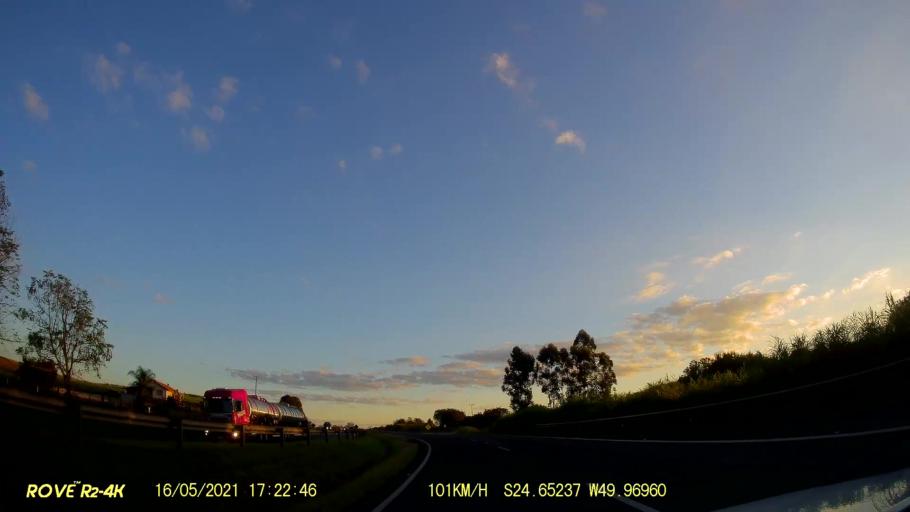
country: BR
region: Parana
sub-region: Pirai Do Sul
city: Pirai do Sul
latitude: -24.6525
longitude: -49.9699
